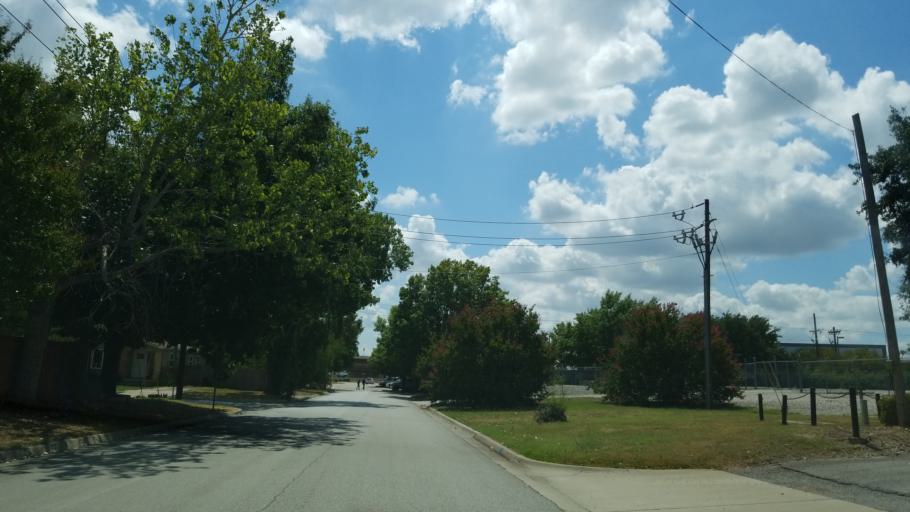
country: US
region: Texas
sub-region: Tarrant County
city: Grapevine
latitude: 32.9263
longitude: -97.0844
